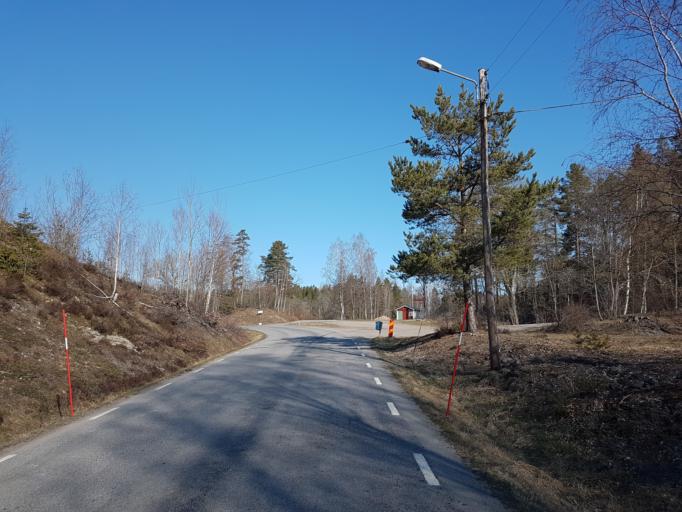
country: SE
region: OEstergoetland
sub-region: Valdemarsviks Kommun
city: Gusum
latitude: 58.1974
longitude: 16.3682
